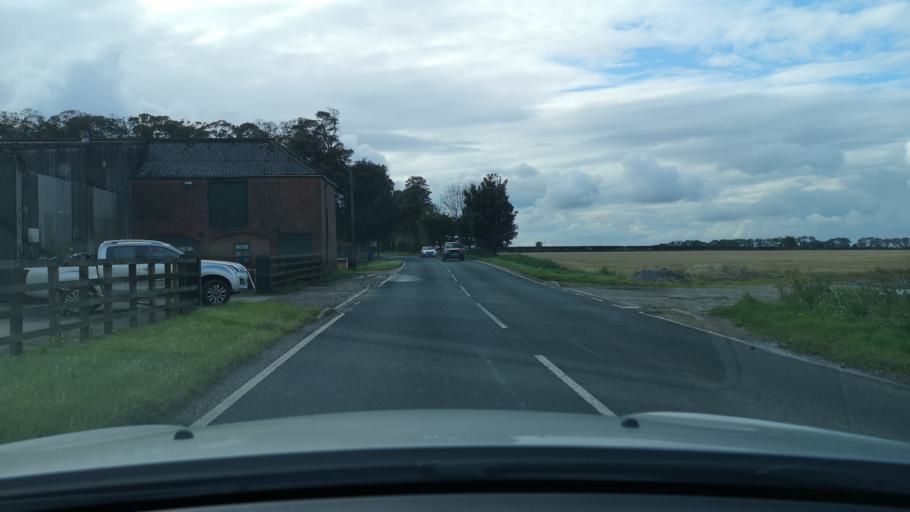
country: GB
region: England
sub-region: East Riding of Yorkshire
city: South Cave
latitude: 53.8046
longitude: -0.5569
